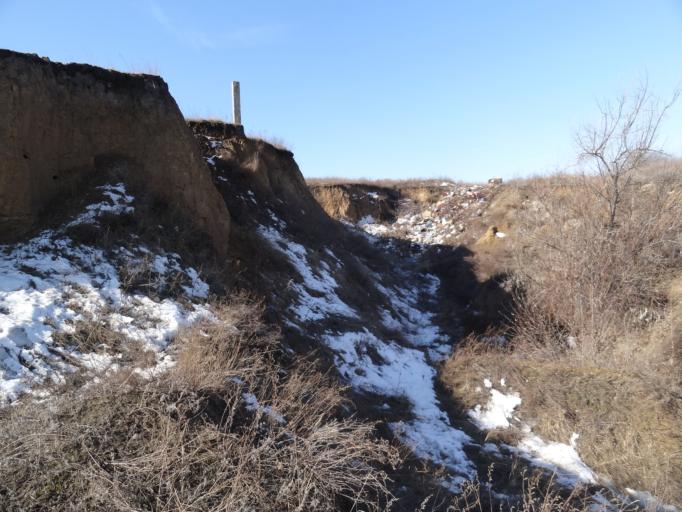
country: RU
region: Saratov
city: Privolzhskiy
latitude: 51.4351
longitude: 45.9616
